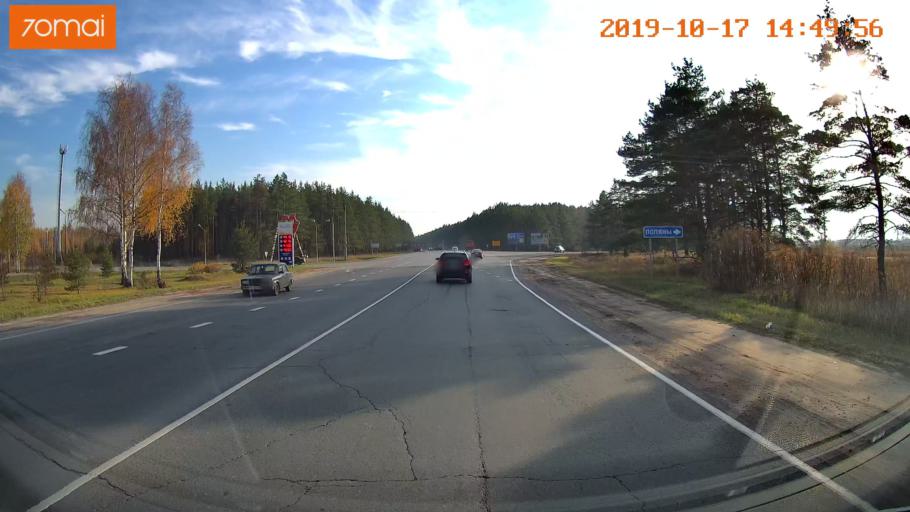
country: RU
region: Rjazan
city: Polyany
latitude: 54.7404
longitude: 39.8407
